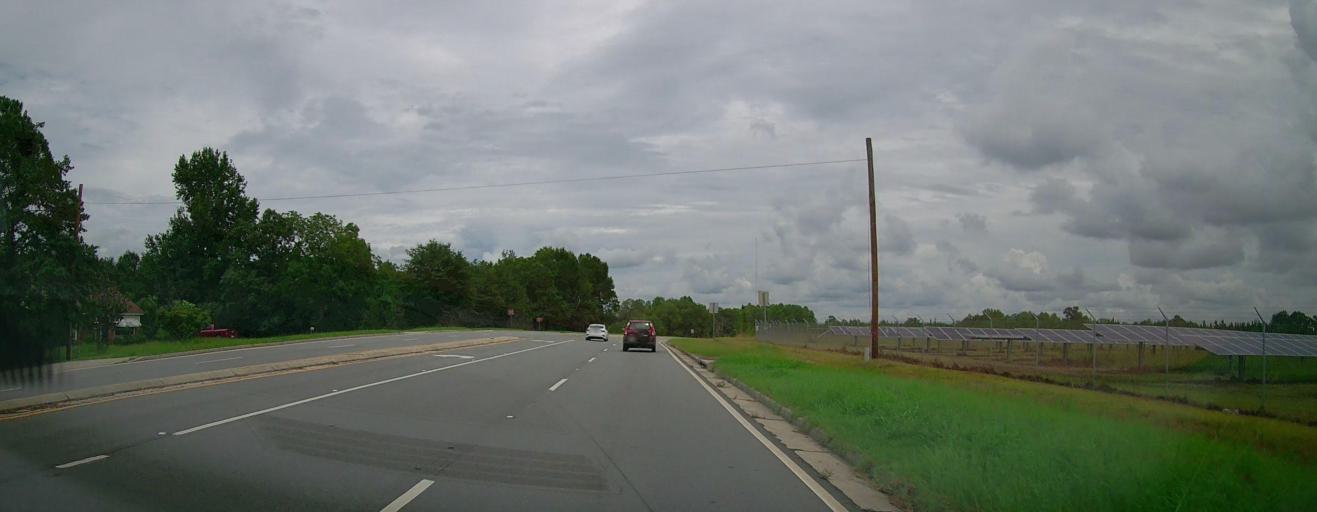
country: US
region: Georgia
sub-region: Telfair County
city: McRae
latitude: 32.0585
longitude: -82.8728
